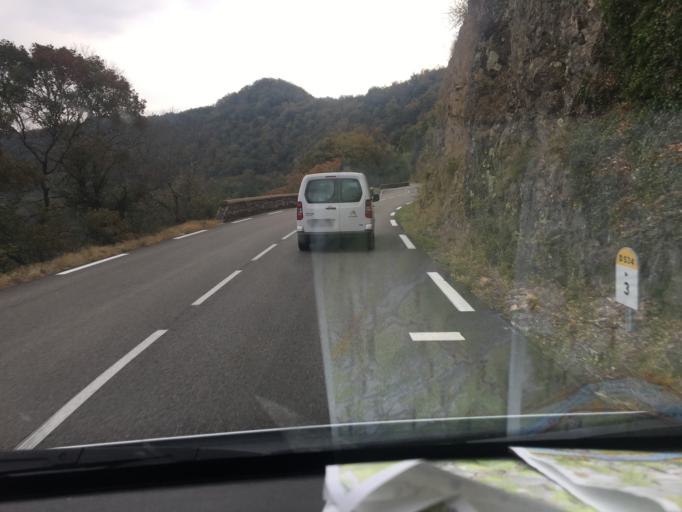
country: FR
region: Rhone-Alpes
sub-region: Departement de l'Ardeche
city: Saint-Jean-de-Muzols
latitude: 45.0579
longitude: 4.7682
